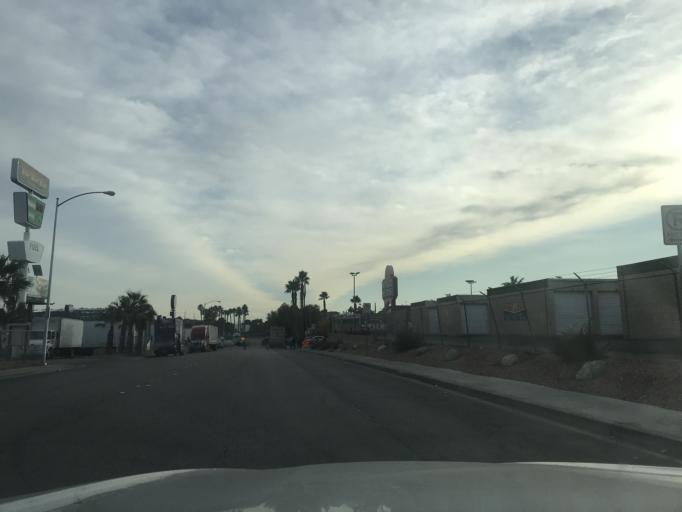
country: US
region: Nevada
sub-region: Clark County
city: Paradise
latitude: 36.1025
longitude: -115.1877
